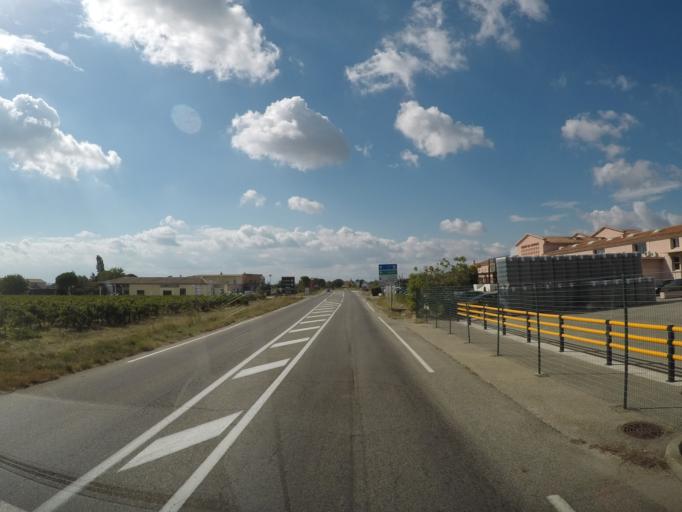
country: FR
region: Rhone-Alpes
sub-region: Departement de la Drome
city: Tulette
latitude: 44.2876
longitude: 4.9442
